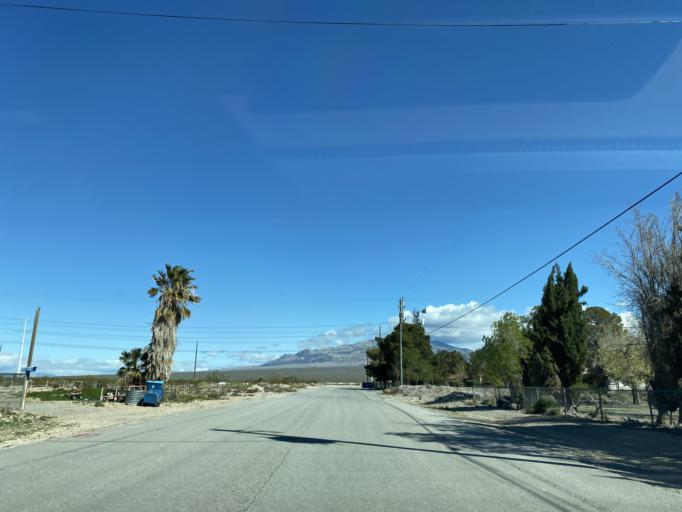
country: US
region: Nevada
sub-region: Clark County
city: North Las Vegas
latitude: 36.3332
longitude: -115.2852
